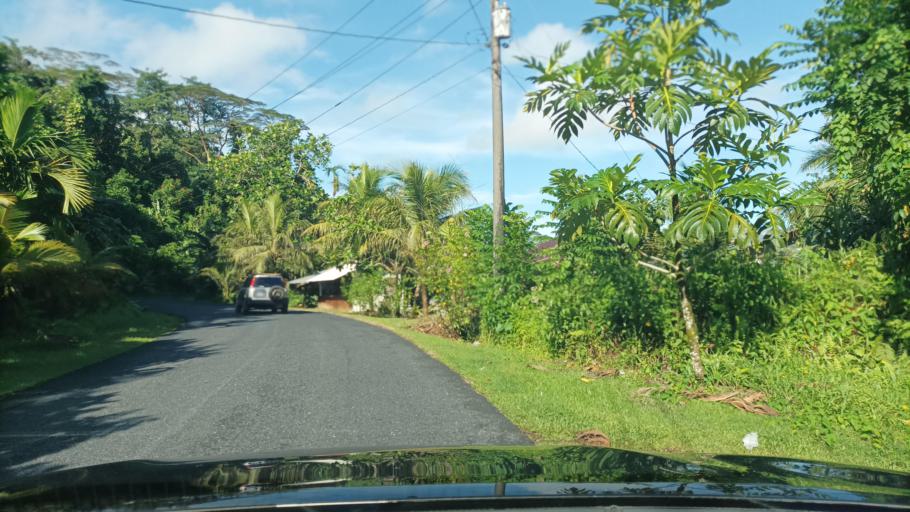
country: FM
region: Pohnpei
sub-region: Kolonia Municipality
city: Kolonia Town
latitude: 6.9516
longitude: 158.1933
